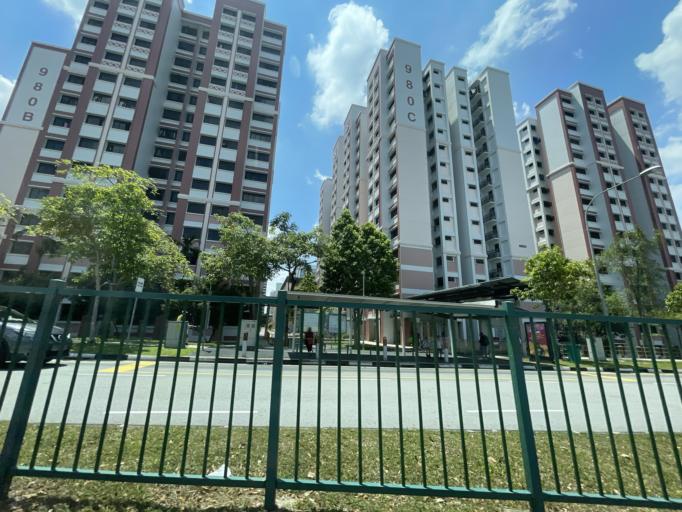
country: MY
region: Johor
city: Kampung Pasir Gudang Baru
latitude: 1.3799
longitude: 103.8815
